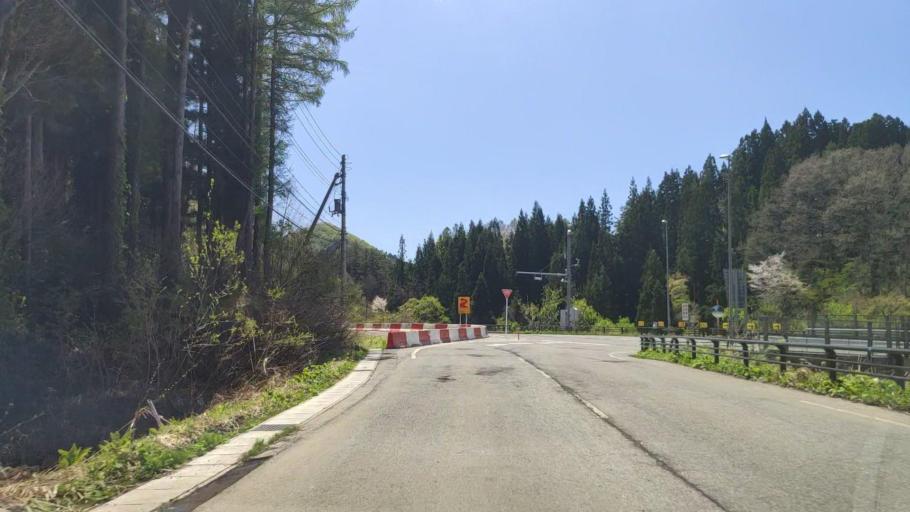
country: JP
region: Yamagata
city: Shinjo
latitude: 38.9164
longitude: 140.3258
